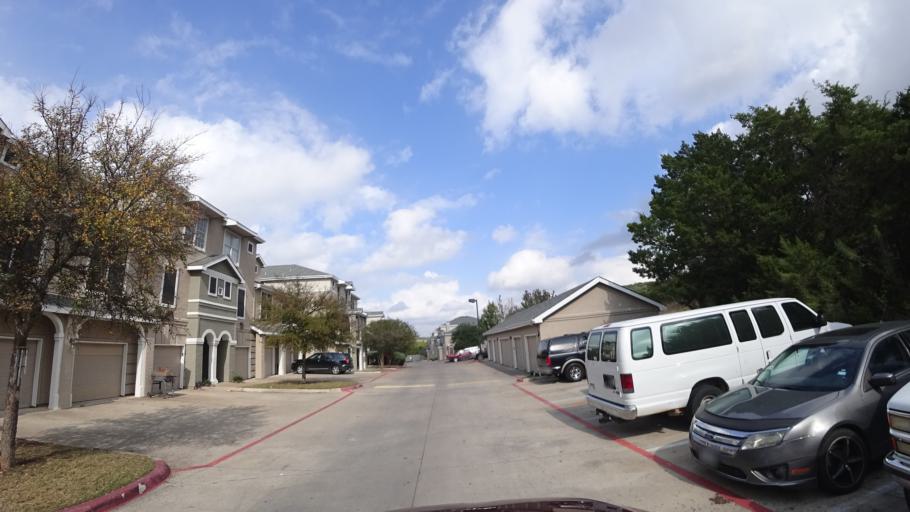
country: US
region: Texas
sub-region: Travis County
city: Hudson Bend
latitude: 30.3841
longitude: -97.8766
